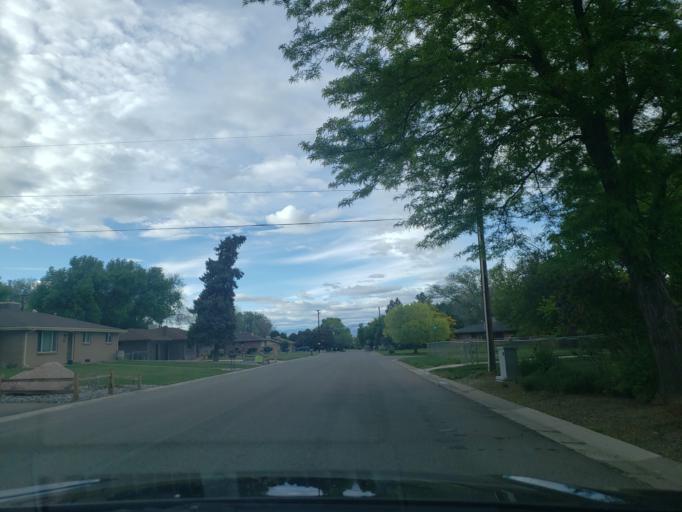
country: US
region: Colorado
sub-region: Mesa County
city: Redlands
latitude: 39.0962
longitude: -108.6586
